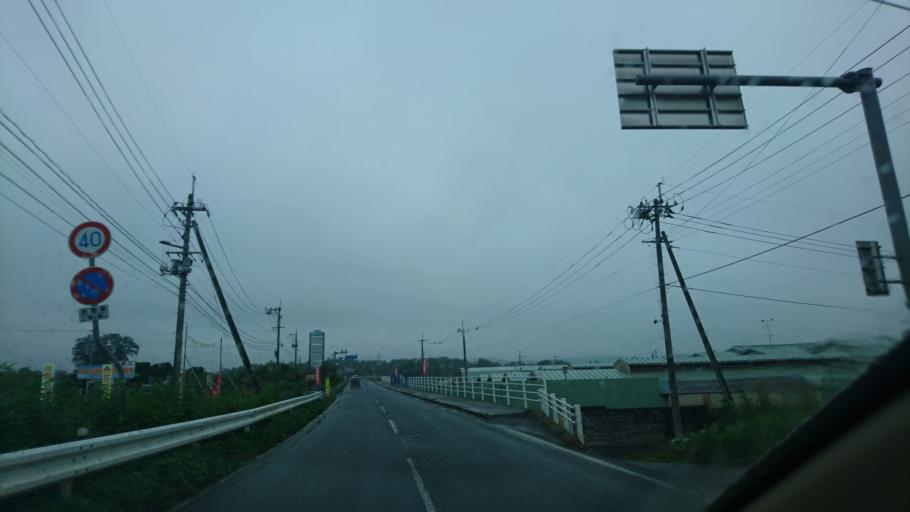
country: JP
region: Iwate
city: Mizusawa
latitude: 39.1353
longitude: 141.1672
